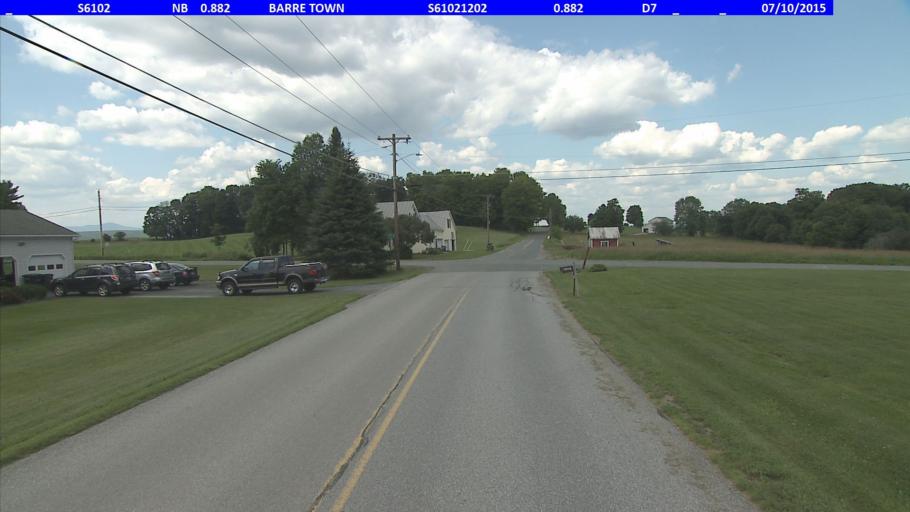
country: US
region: Vermont
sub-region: Washington County
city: Barre
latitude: 44.2246
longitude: -72.5089
